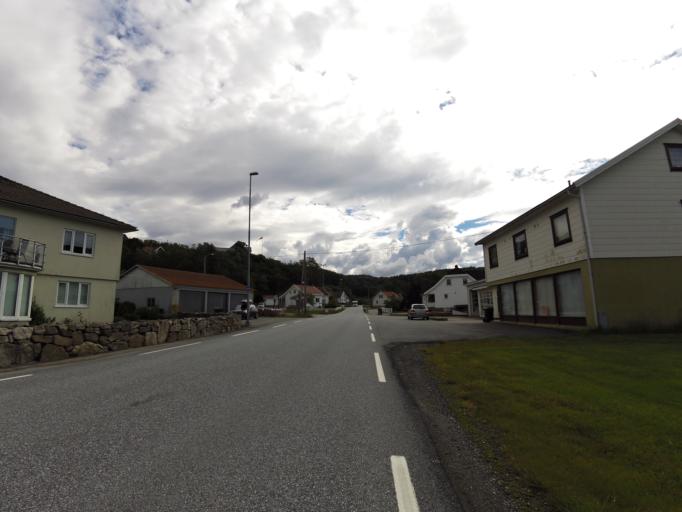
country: NO
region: Vest-Agder
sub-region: Lindesnes
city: Vigeland
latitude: 58.0510
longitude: 7.1910
